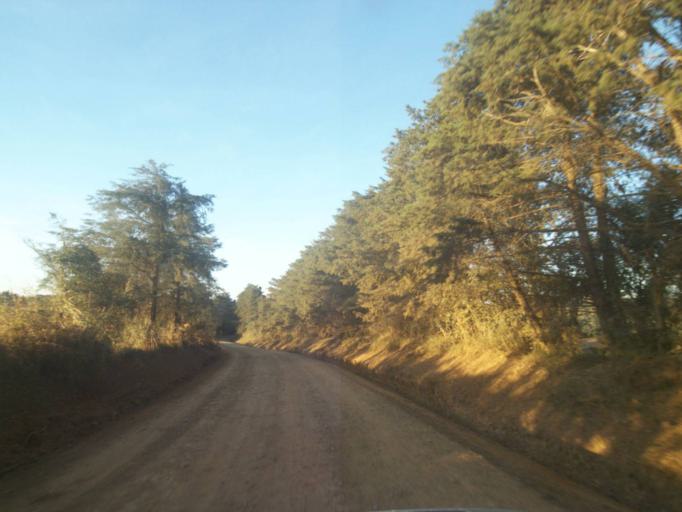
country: BR
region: Parana
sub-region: Tibagi
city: Tibagi
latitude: -24.5277
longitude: -50.5107
